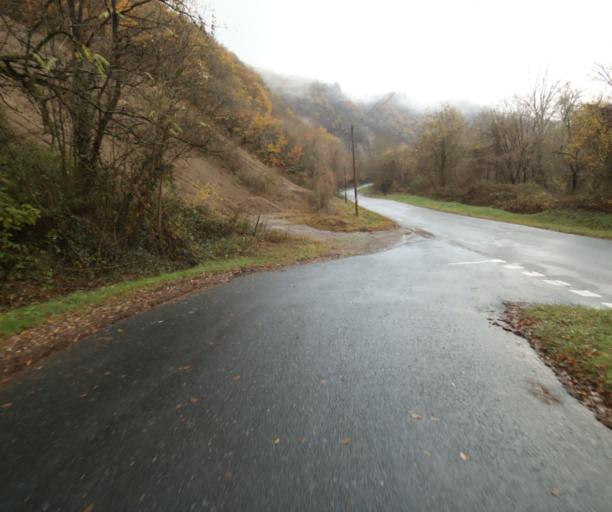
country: FR
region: Limousin
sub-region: Departement de la Correze
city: Cornil
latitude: 45.1867
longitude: 1.6546
